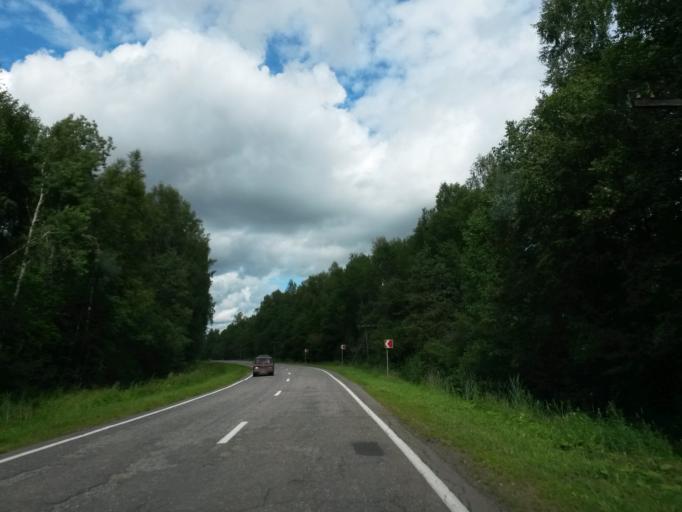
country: RU
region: Jaroslavl
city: Tutayev
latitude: 57.9167
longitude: 39.5154
